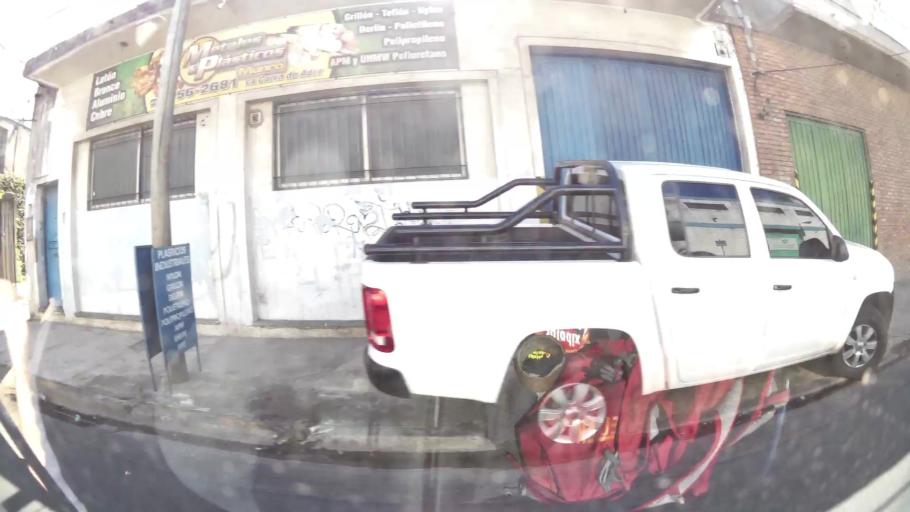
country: AR
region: Buenos Aires
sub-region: Partido de General San Martin
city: General San Martin
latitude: -34.5356
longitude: -58.5411
